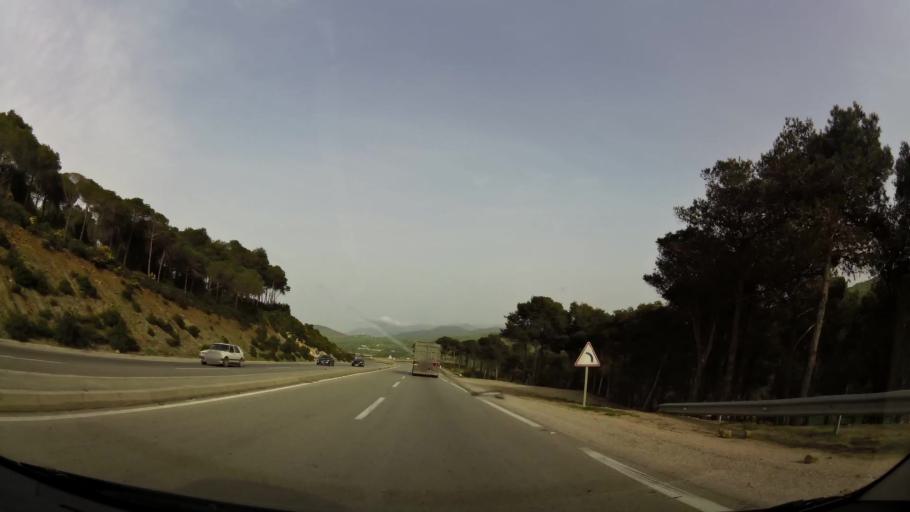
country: MA
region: Tanger-Tetouan
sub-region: Tetouan
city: Saddina
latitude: 35.5461
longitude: -5.5599
